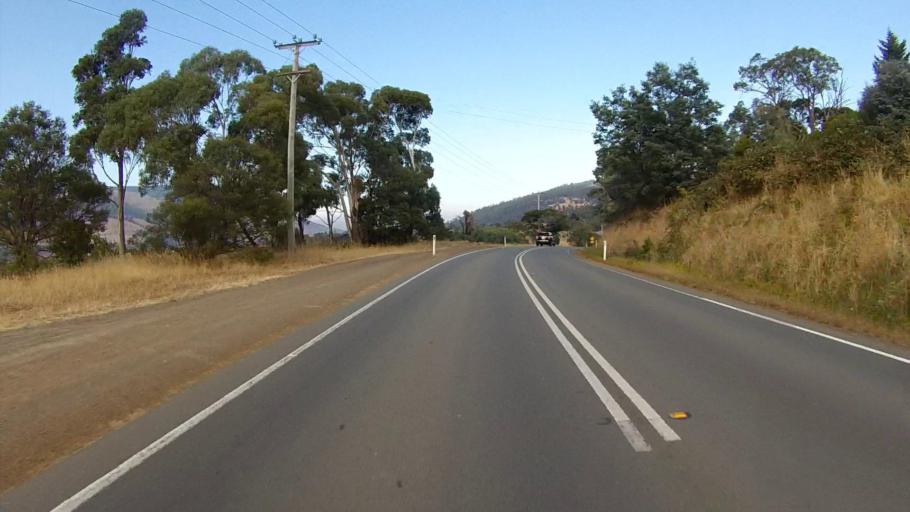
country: AU
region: Tasmania
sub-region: Brighton
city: Bridgewater
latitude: -42.7272
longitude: 147.1880
